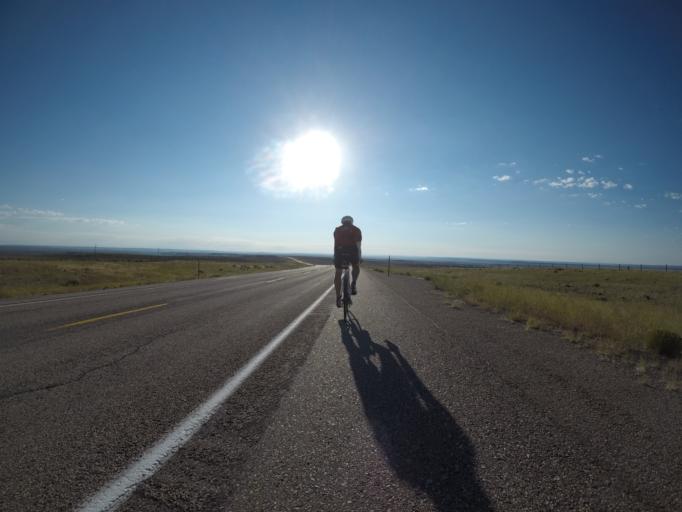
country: US
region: Wyoming
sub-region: Lincoln County
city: Kemmerer
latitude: 41.8856
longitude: -110.3758
